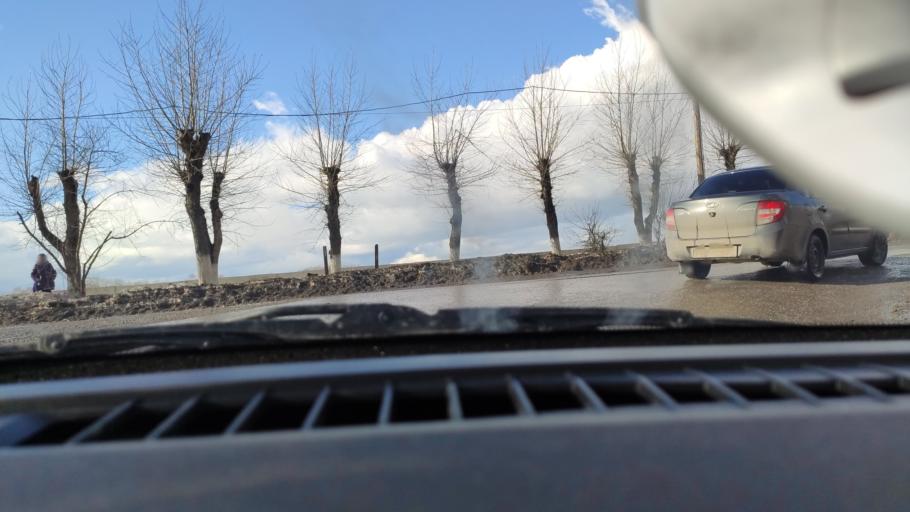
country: RU
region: Perm
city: Nytva
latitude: 57.9339
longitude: 55.3231
